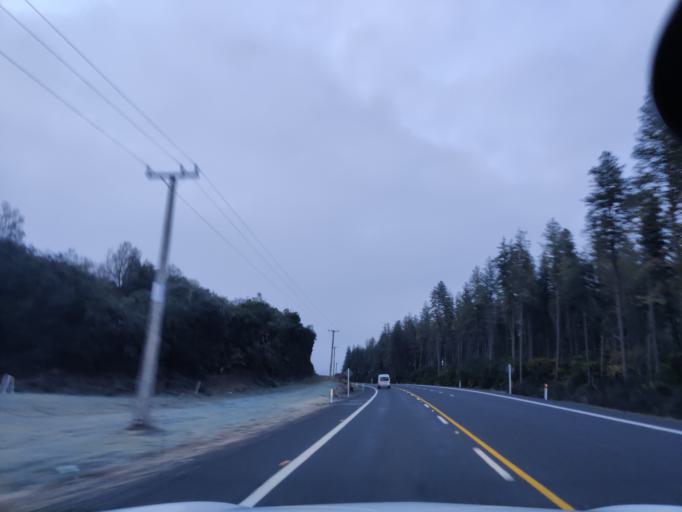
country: NZ
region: Waikato
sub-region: South Waikato District
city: Tokoroa
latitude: -38.3816
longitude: 176.0037
